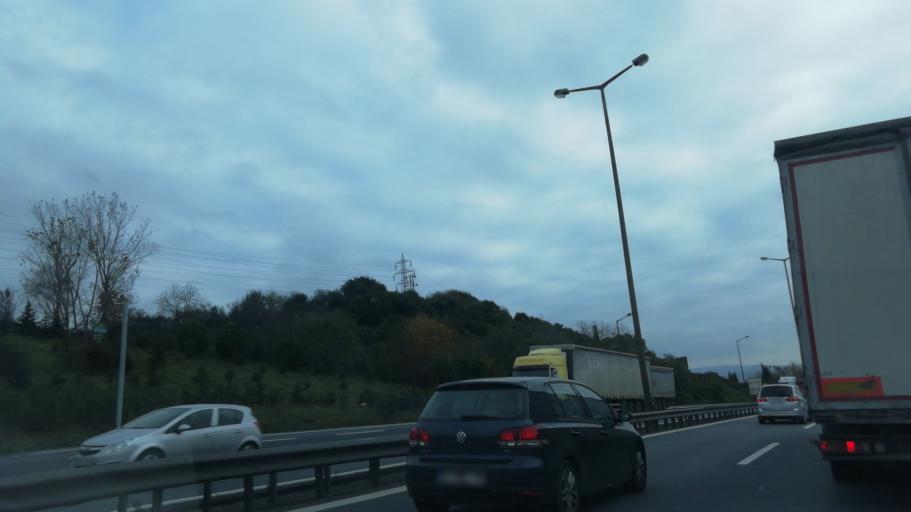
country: TR
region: Kocaeli
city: Izmit
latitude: 40.7837
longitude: 29.9309
